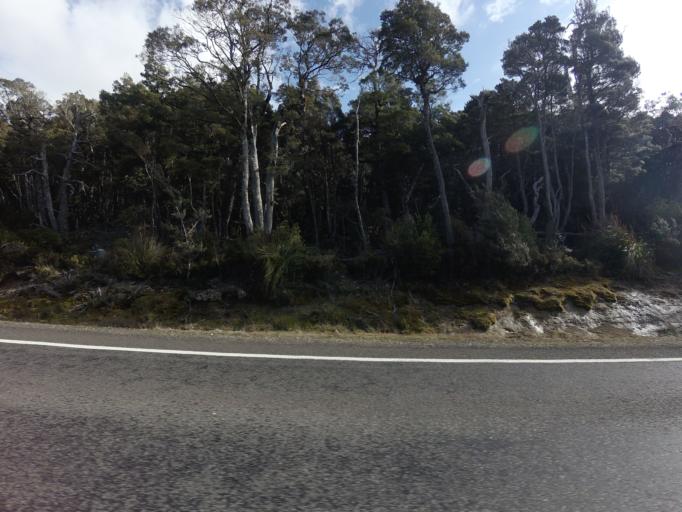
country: AU
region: Tasmania
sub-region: Meander Valley
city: Deloraine
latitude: -41.7093
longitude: 146.7280
